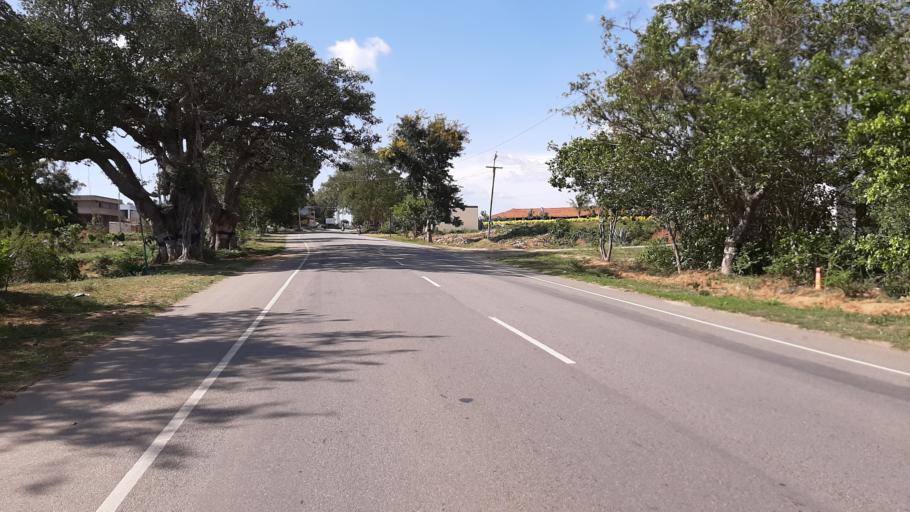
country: IN
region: Tamil Nadu
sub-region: Krishnagiri
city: Denkanikota
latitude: 12.5466
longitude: 77.7869
